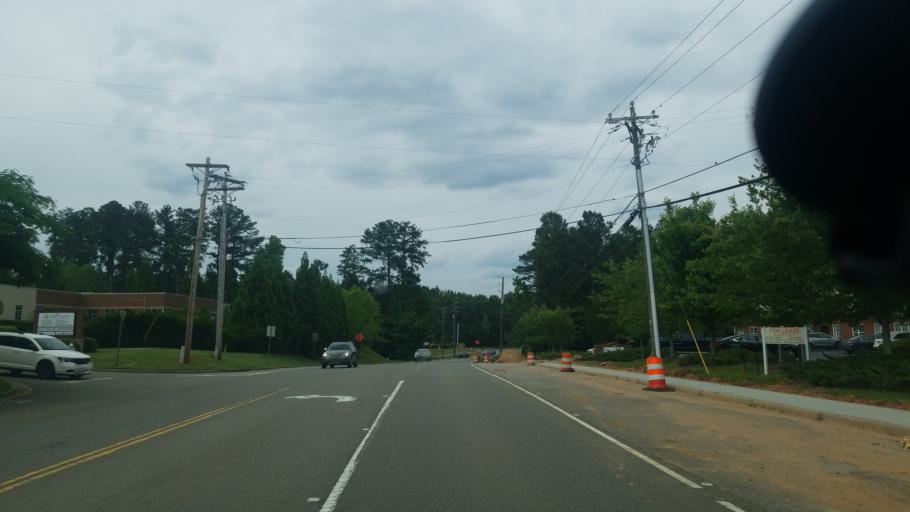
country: US
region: Georgia
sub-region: Forsyth County
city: Cumming
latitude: 34.1839
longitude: -84.1236
